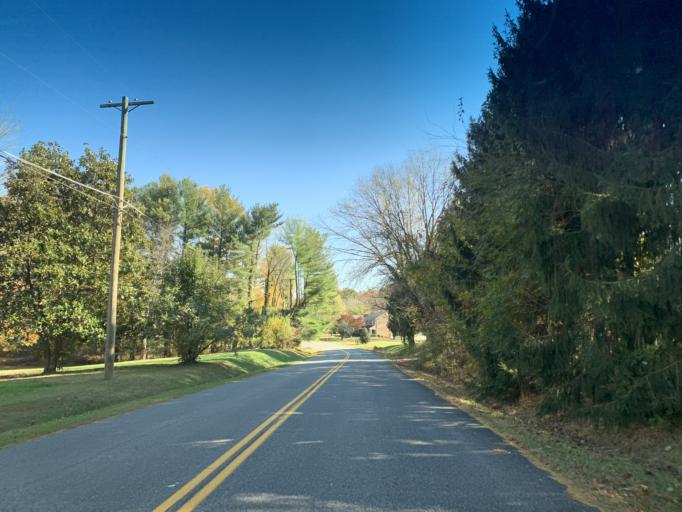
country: US
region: Maryland
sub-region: Harford County
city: Joppatowne
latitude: 39.4734
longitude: -76.3639
